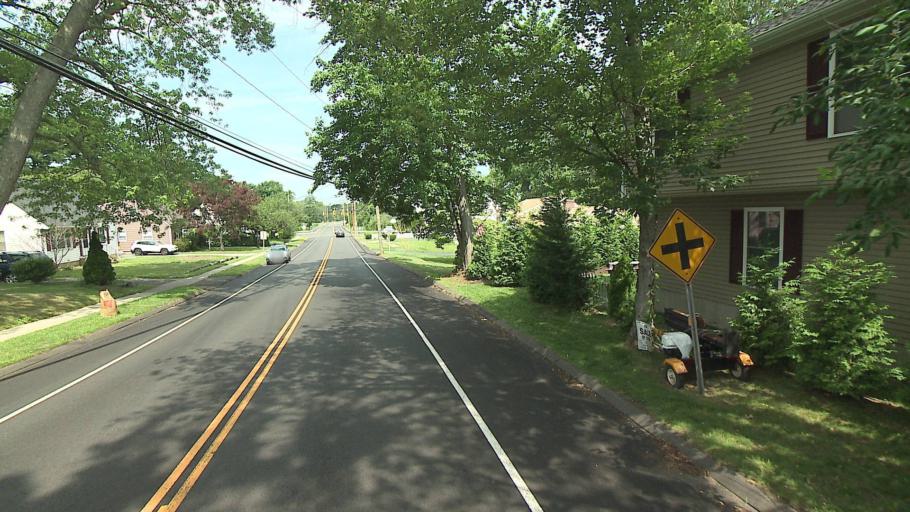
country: US
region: Connecticut
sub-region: New Haven County
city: Milford
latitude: 41.2153
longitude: -73.0335
